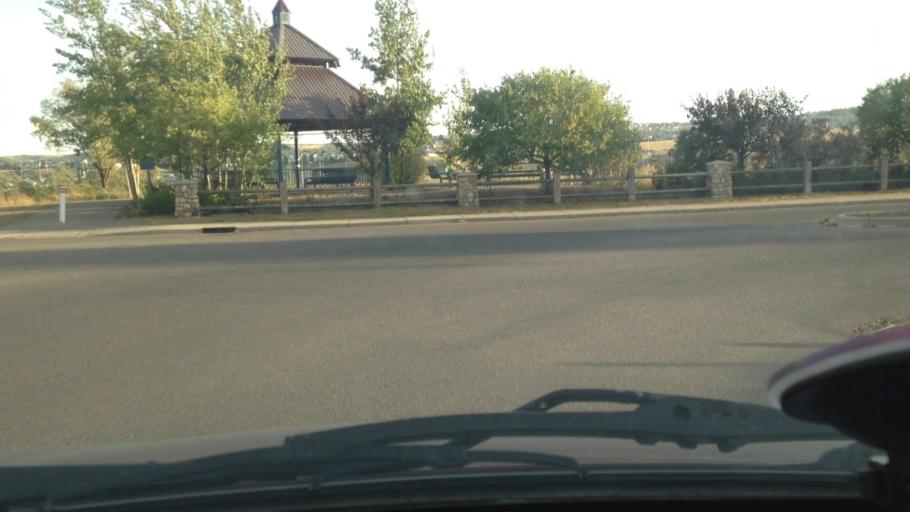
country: CA
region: Alberta
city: Calgary
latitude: 51.1617
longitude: -114.1168
